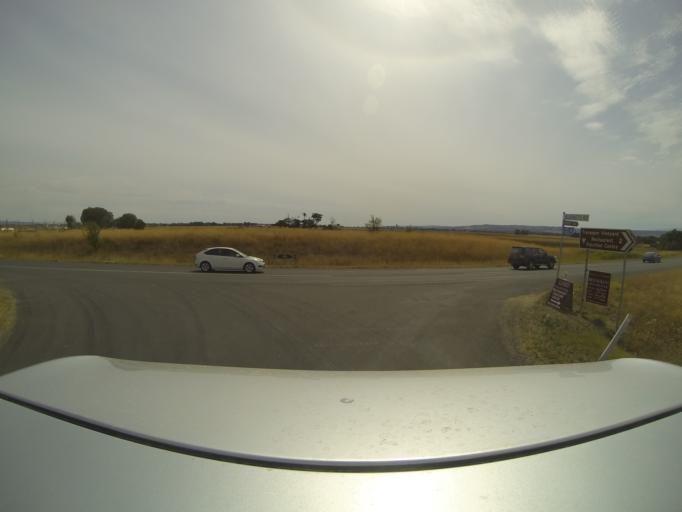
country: AU
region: Victoria
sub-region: Latrobe
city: Traralgon
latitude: -38.1691
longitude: 146.5648
